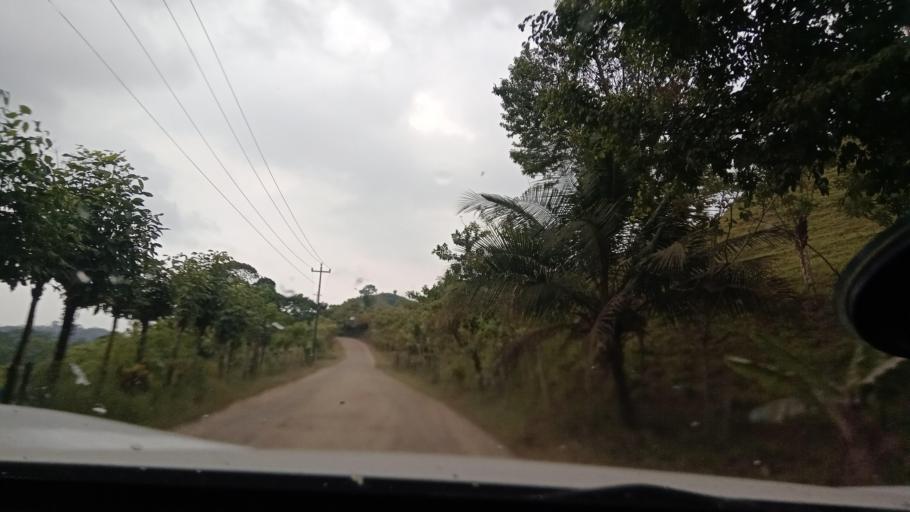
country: MX
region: Tabasco
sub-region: Huimanguillo
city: Francisco Rueda
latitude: 17.4460
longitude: -94.0752
